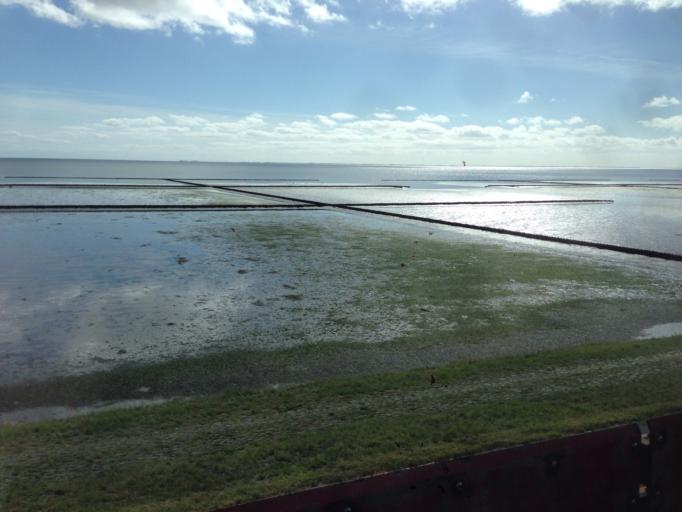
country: DE
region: Schleswig-Holstein
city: Sylt-Ost
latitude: 54.8806
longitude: 8.5018
